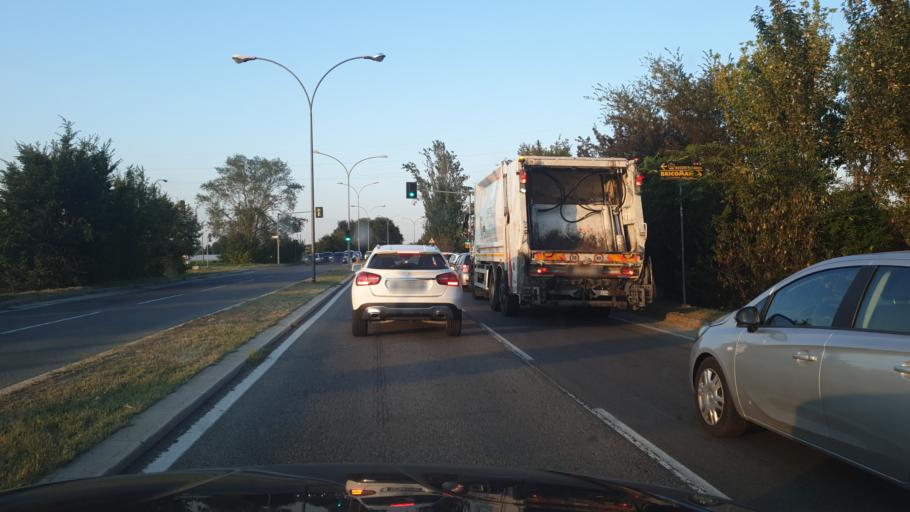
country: IT
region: Emilia-Romagna
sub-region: Provincia di Bologna
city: Quarto Inferiore
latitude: 44.5175
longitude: 11.3814
